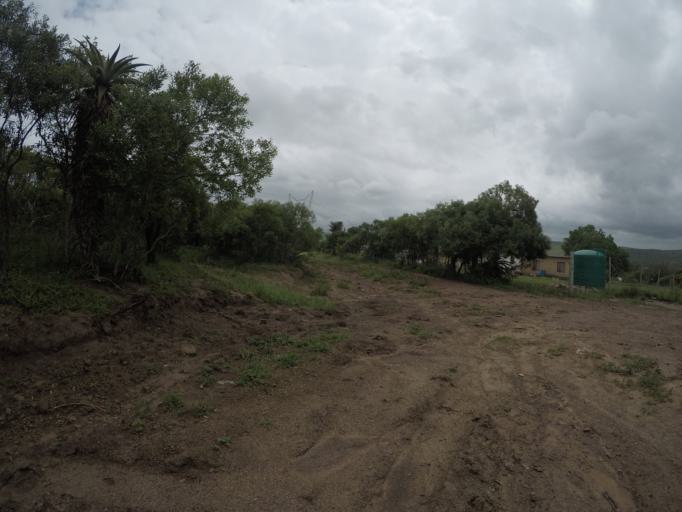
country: ZA
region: KwaZulu-Natal
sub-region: uThungulu District Municipality
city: Empangeni
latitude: -28.6054
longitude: 31.8297
